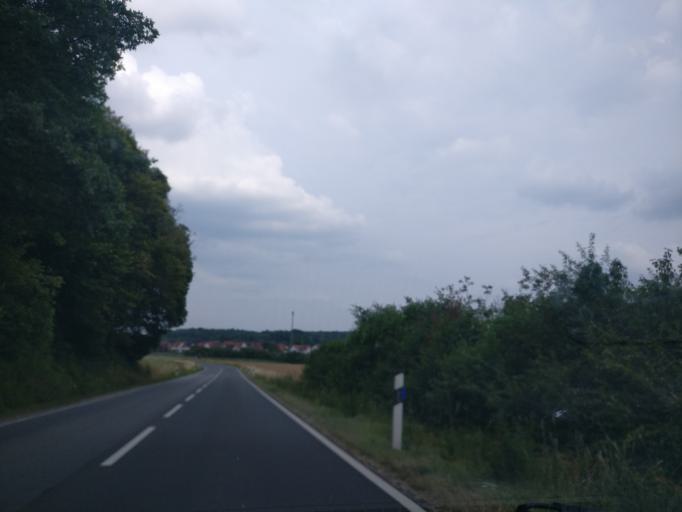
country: DE
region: Lower Saxony
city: Adelebsen
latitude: 51.5872
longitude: 9.7967
